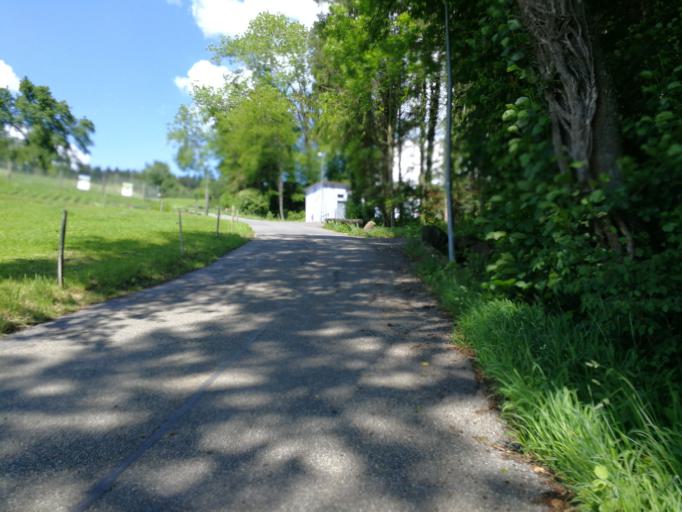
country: CH
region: Zurich
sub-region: Bezirk Meilen
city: Uetikon / Grossdorf
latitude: 47.2762
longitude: 8.6855
